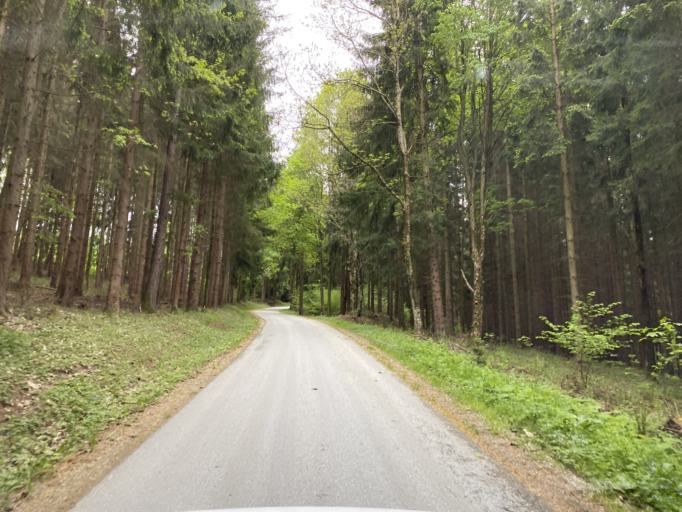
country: AT
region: Styria
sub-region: Politischer Bezirk Weiz
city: Baierdorf-Umgebung
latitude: 47.3106
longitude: 15.7092
